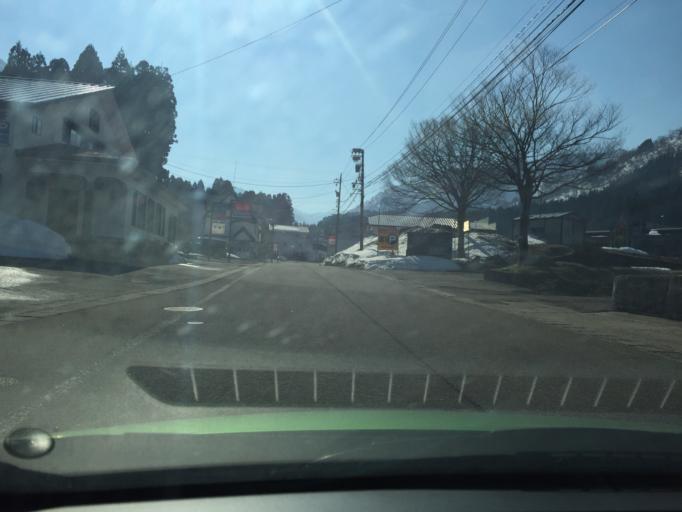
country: JP
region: Ishikawa
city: Tsurugi-asahimachi
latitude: 36.2696
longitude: 136.7144
